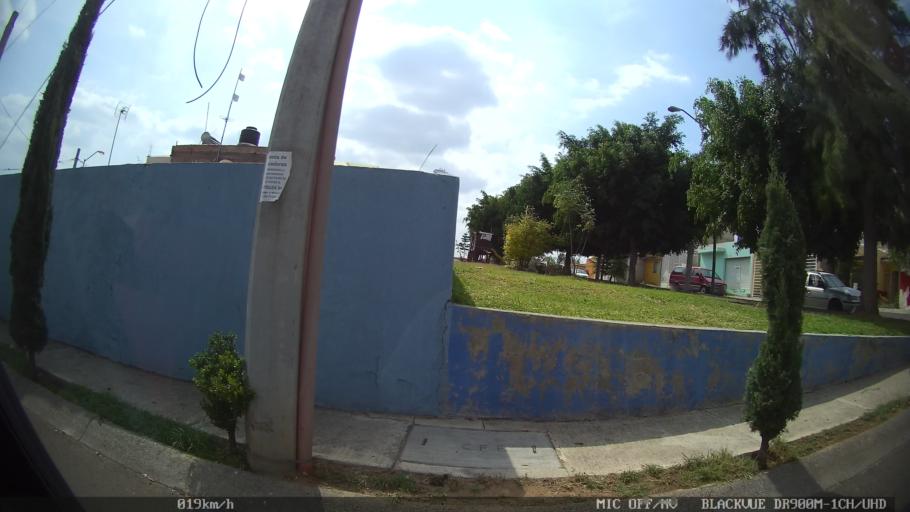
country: MX
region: Jalisco
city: Coyula
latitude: 20.6416
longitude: -103.2174
